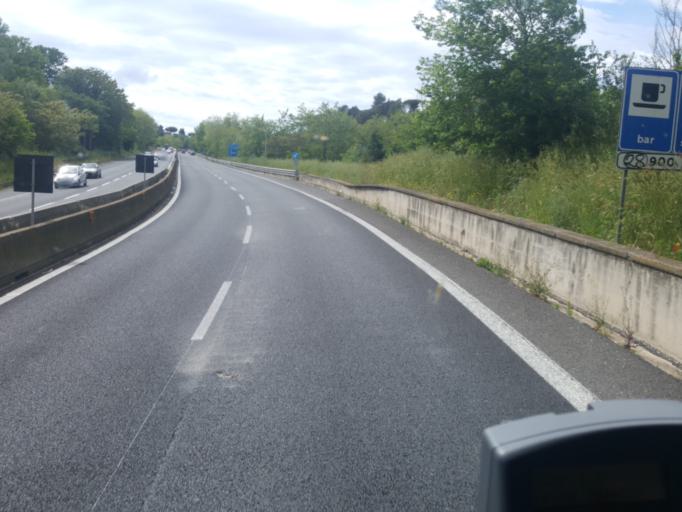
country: IT
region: Latium
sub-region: Citta metropolitana di Roma Capitale
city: Ara Nova
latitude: 41.9100
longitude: 12.2598
